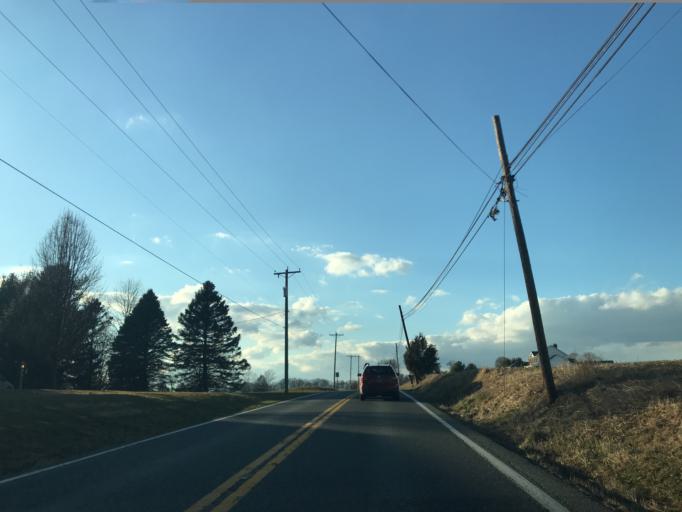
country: US
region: Pennsylvania
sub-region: York County
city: Susquehanna Trails
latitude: 39.7153
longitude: -76.3552
